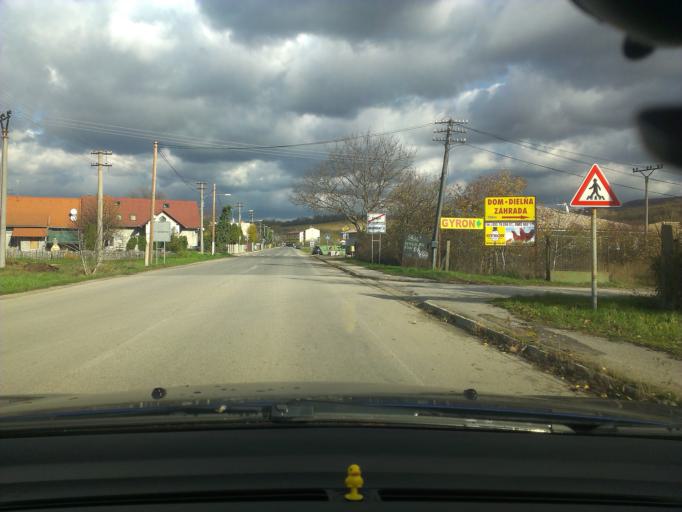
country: SK
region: Trnavsky
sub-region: Okres Trnava
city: Piestany
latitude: 48.5925
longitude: 17.8570
